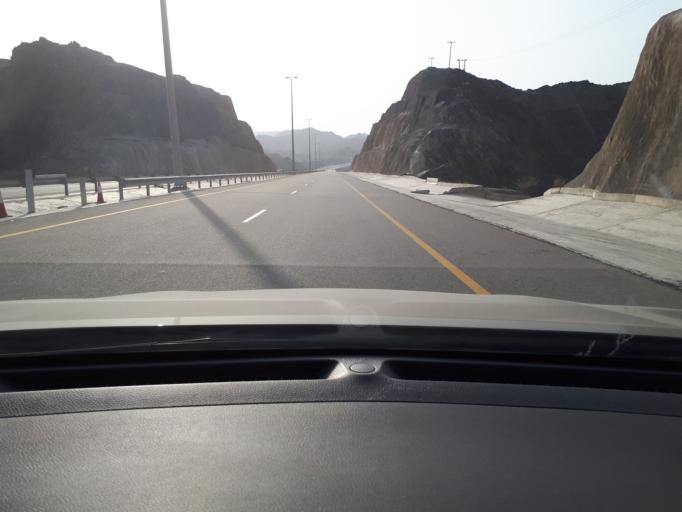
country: OM
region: Muhafazat Masqat
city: Muscat
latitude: 23.2086
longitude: 58.8062
